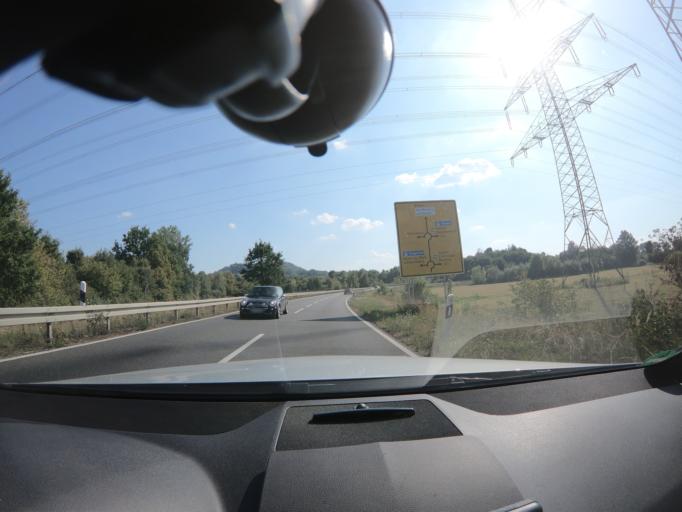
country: DE
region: Hesse
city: Amoneburg
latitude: 50.8124
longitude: 8.9174
